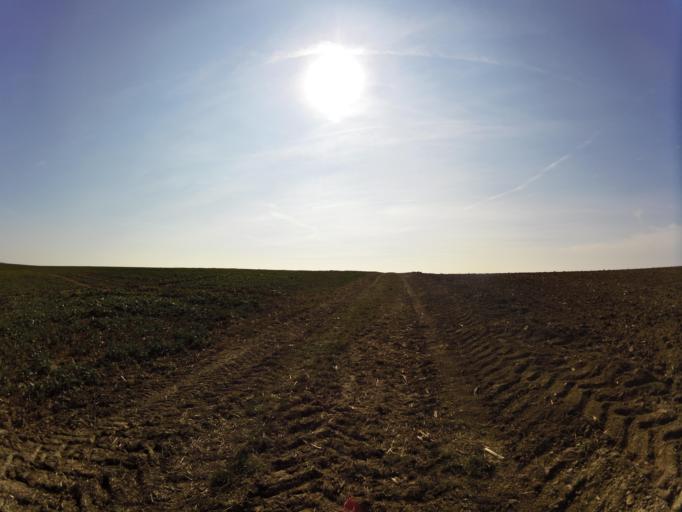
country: DE
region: Bavaria
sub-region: Regierungsbezirk Unterfranken
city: Dettelbach
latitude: 49.8298
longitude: 10.1430
